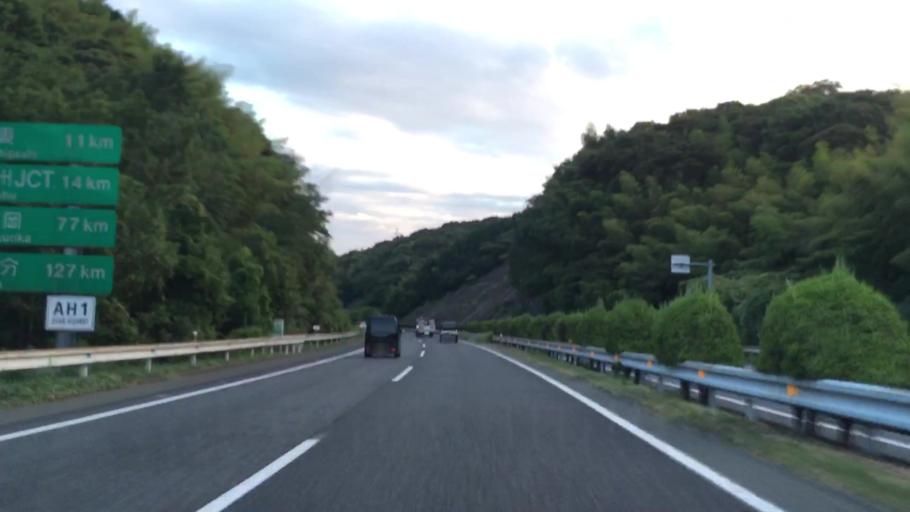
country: JP
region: Yamaguchi
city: Shimonoseki
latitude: 33.9049
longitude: 130.9719
